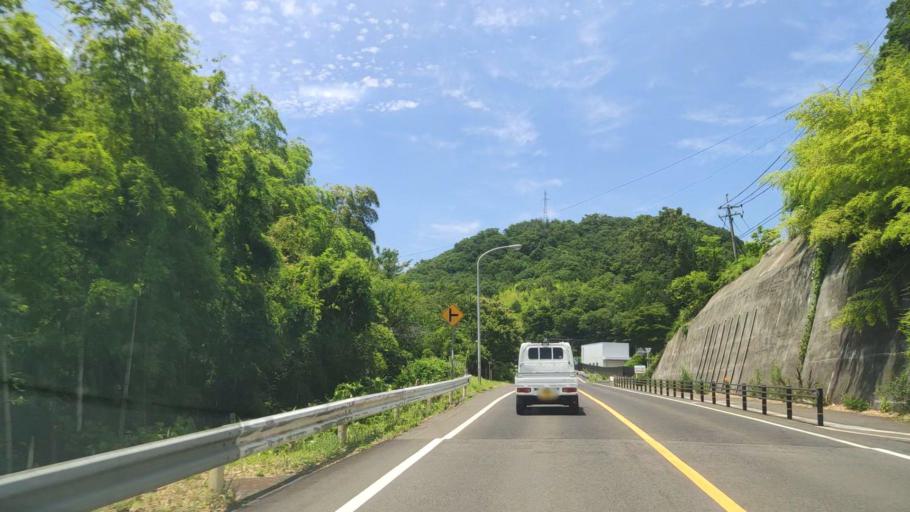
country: JP
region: Tottori
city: Tottori
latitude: 35.3997
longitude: 134.2670
